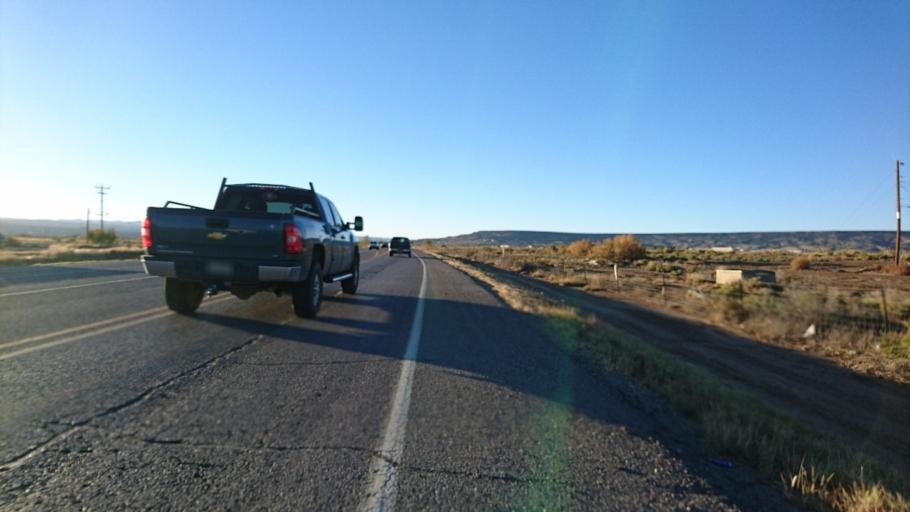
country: US
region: New Mexico
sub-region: Cibola County
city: Grants
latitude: 35.1308
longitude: -107.8108
